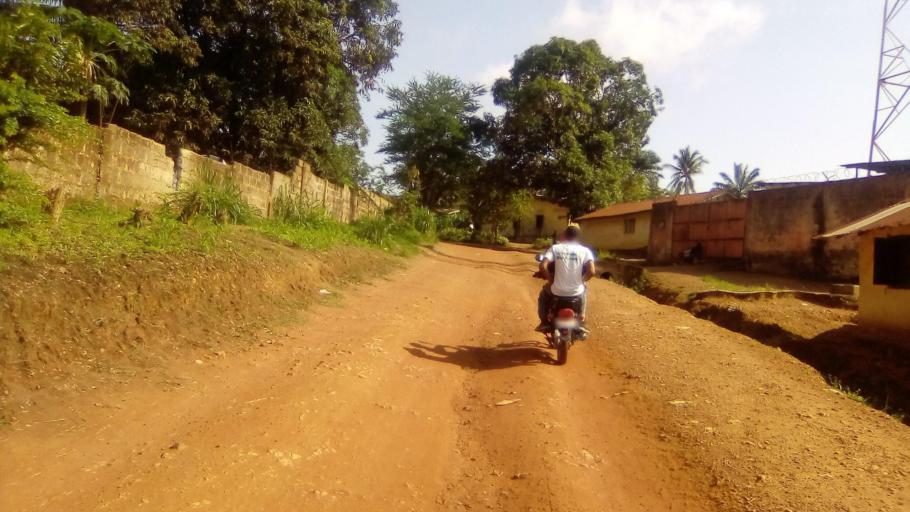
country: SL
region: Southern Province
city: Bo
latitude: 7.9712
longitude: -11.7313
